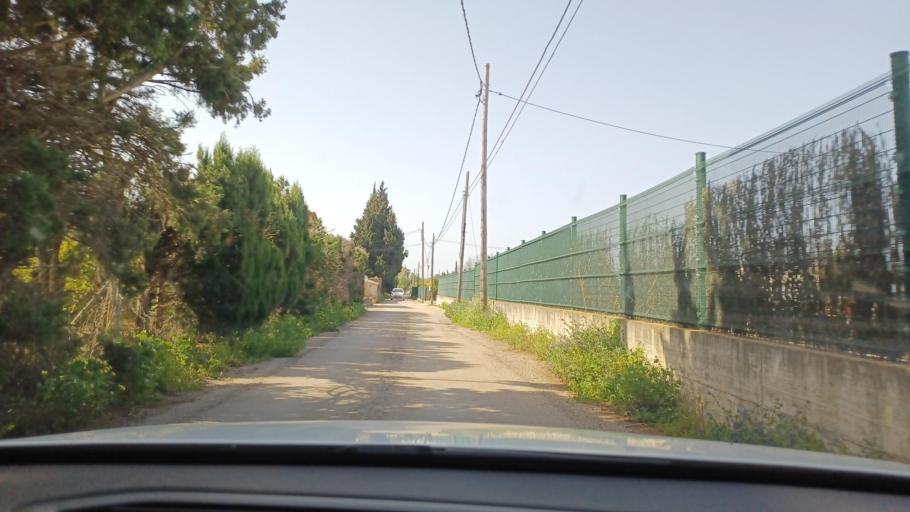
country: ES
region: Catalonia
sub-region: Provincia de Tarragona
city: Tortosa
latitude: 40.7961
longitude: 0.5164
